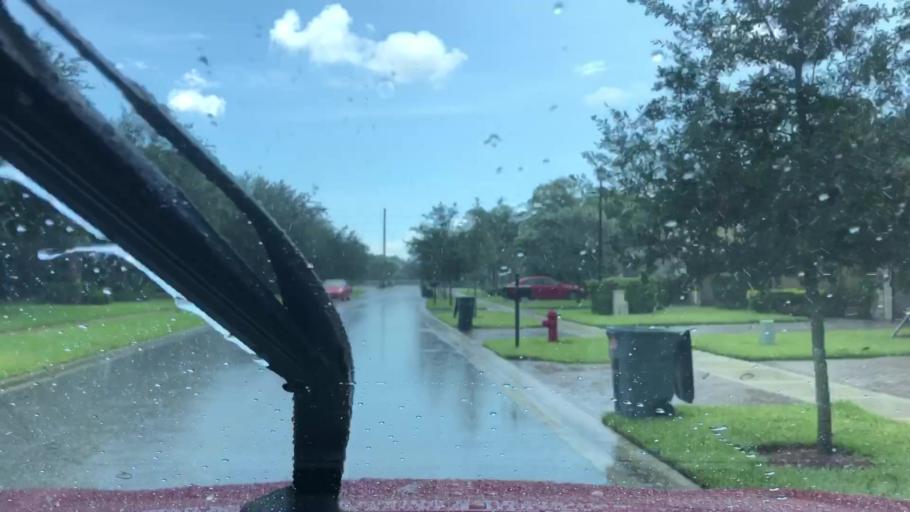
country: US
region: Florida
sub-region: Palm Beach County
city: Seminole Manor
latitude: 26.5599
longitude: -80.1169
